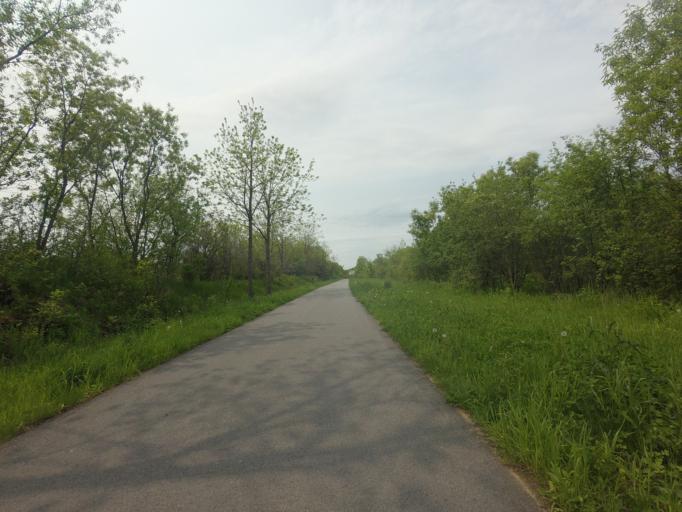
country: CA
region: Ontario
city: Kingston
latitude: 44.2552
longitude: -76.4913
